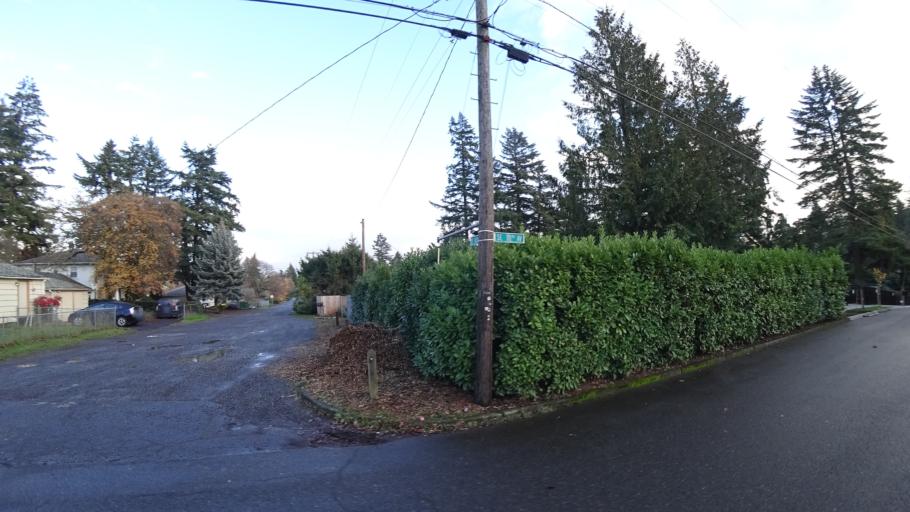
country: US
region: Oregon
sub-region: Multnomah County
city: Lents
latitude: 45.5175
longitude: -122.5494
